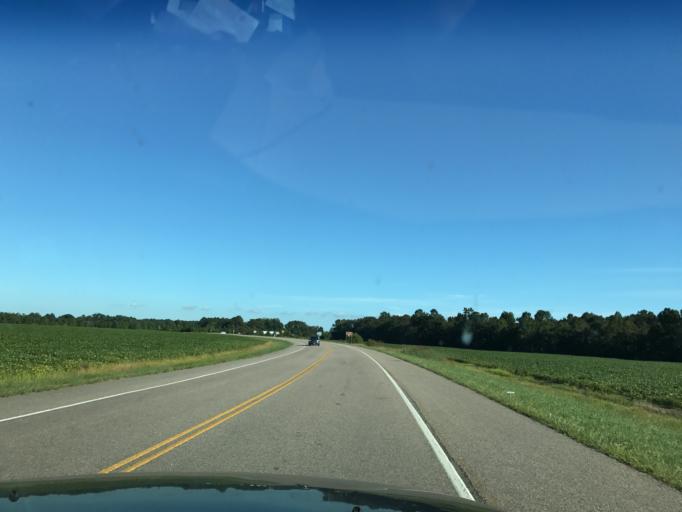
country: US
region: Virginia
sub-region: City of Portsmouth
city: Portsmouth Heights
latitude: 36.6901
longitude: -76.3532
